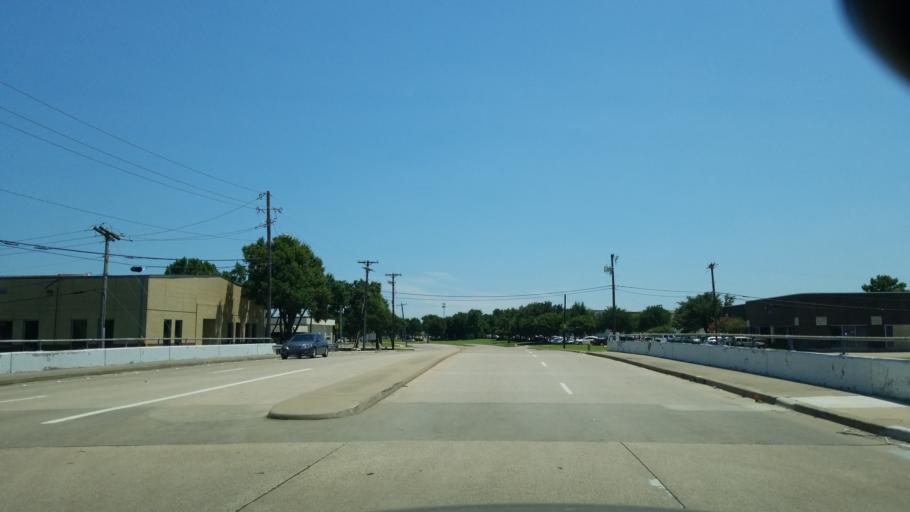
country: US
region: Texas
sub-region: Dallas County
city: Farmers Branch
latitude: 32.9418
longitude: -96.9167
